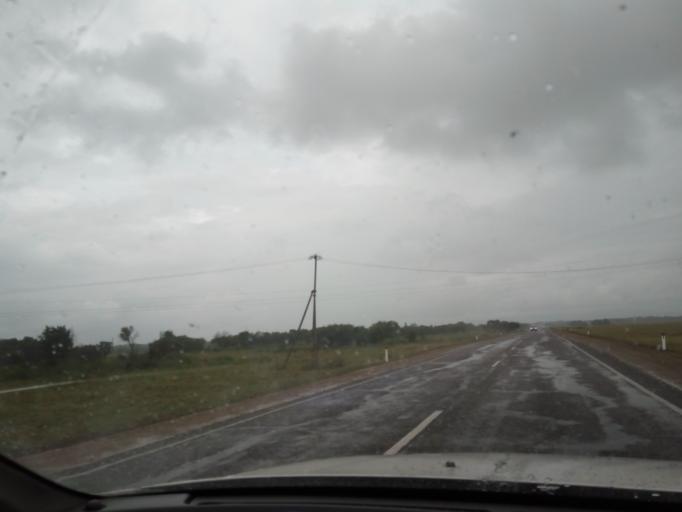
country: RU
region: Primorskiy
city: Dal'nerechensk
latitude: 45.9083
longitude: 133.7584
